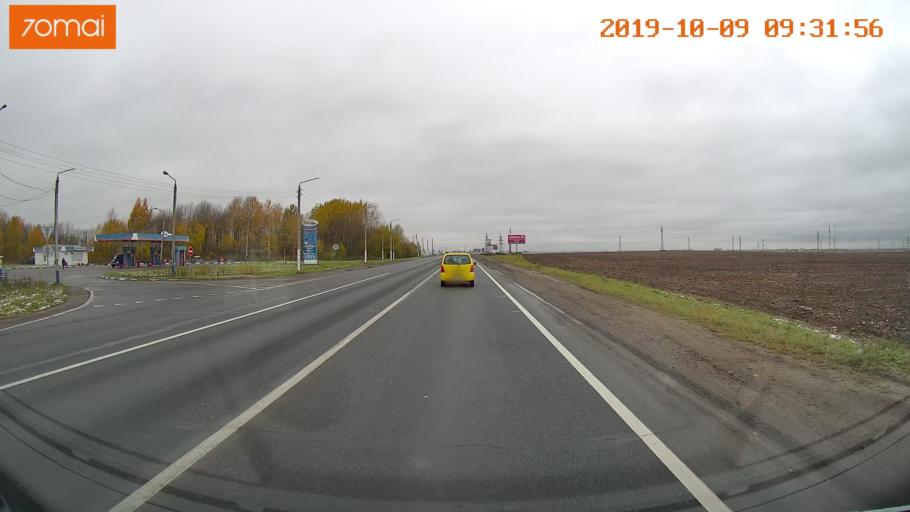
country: RU
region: Vologda
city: Vologda
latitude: 59.1539
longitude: 39.9339
